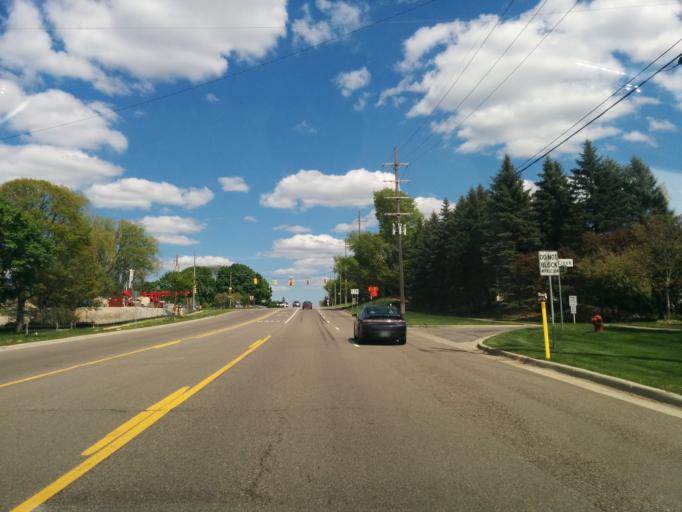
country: US
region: Michigan
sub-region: Oakland County
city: Franklin
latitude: 42.5142
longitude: -83.3414
